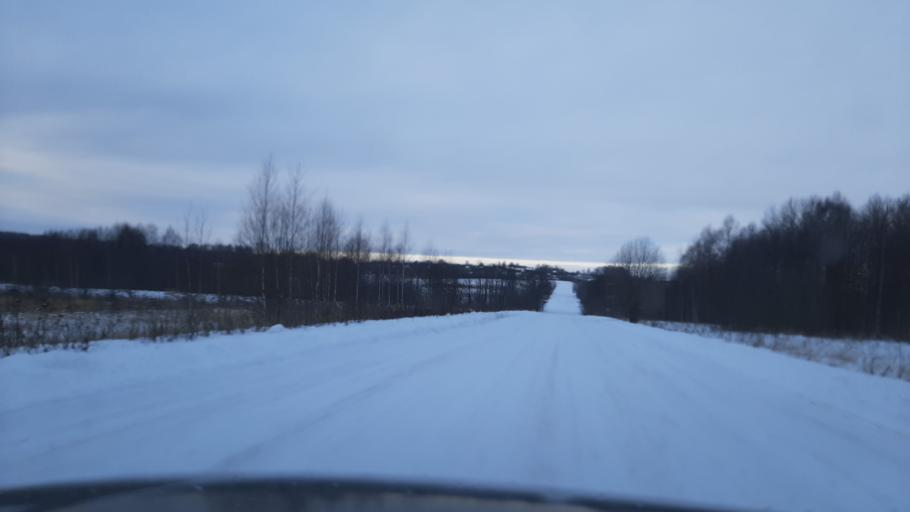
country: RU
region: Kostroma
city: Volgorechensk
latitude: 57.4480
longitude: 40.9861
